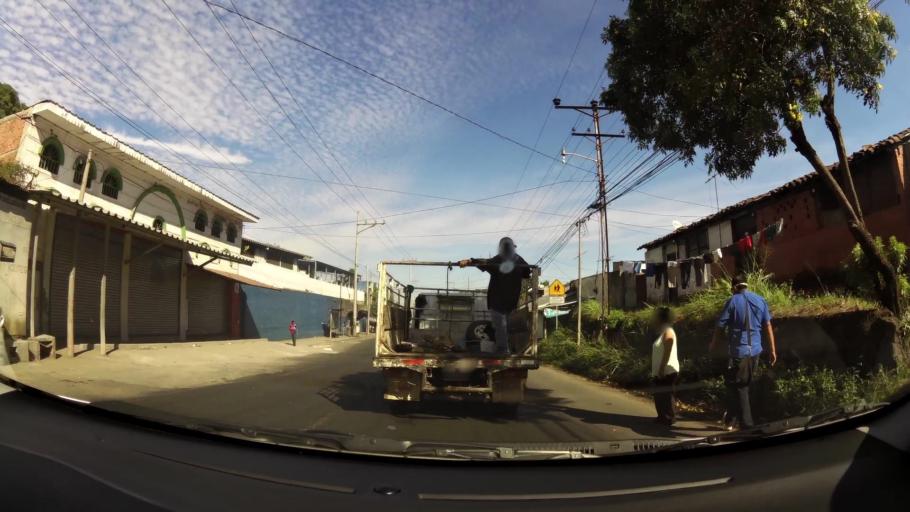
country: SV
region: Santa Ana
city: Santa Ana
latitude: 13.9820
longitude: -89.5770
